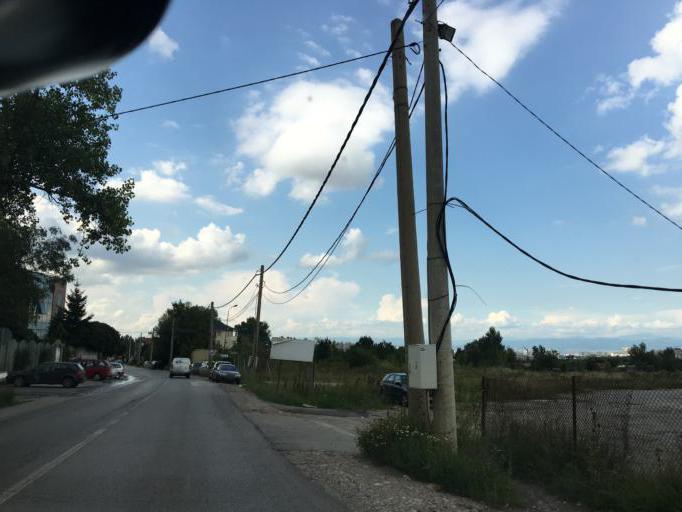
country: BG
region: Sofia-Capital
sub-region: Stolichna Obshtina
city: Sofia
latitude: 42.6280
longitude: 23.3579
